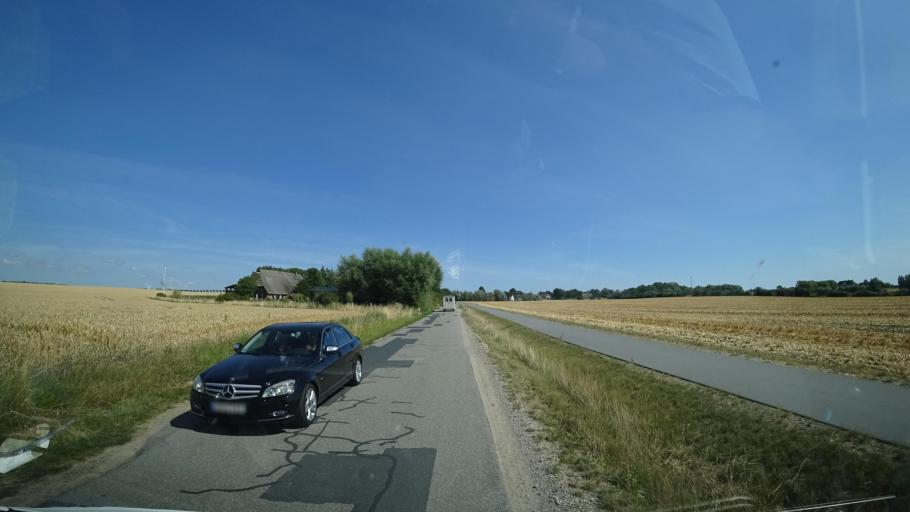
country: DE
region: Mecklenburg-Vorpommern
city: Blowatz
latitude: 54.0221
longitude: 11.5543
